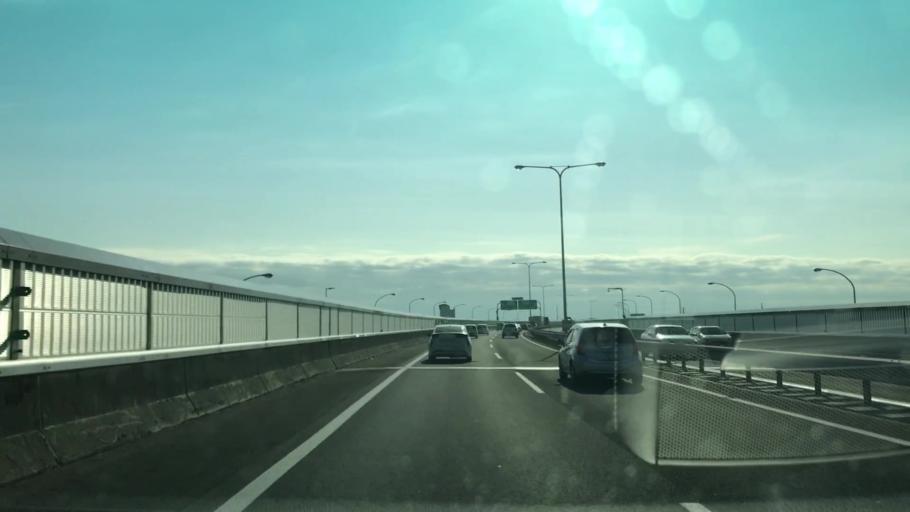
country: JP
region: Hokkaido
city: Sapporo
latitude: 43.0864
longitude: 141.4168
